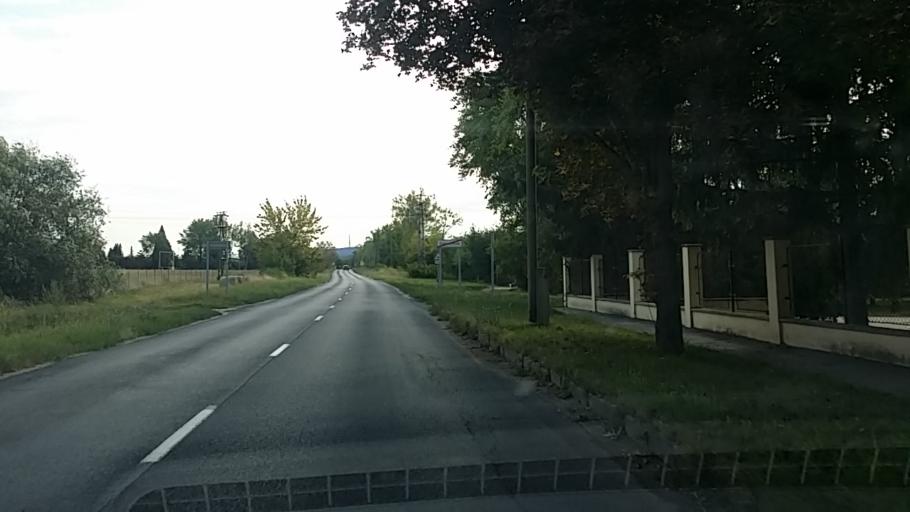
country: HU
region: Gyor-Moson-Sopron
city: Fertorakos
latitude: 47.7223
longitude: 16.6198
